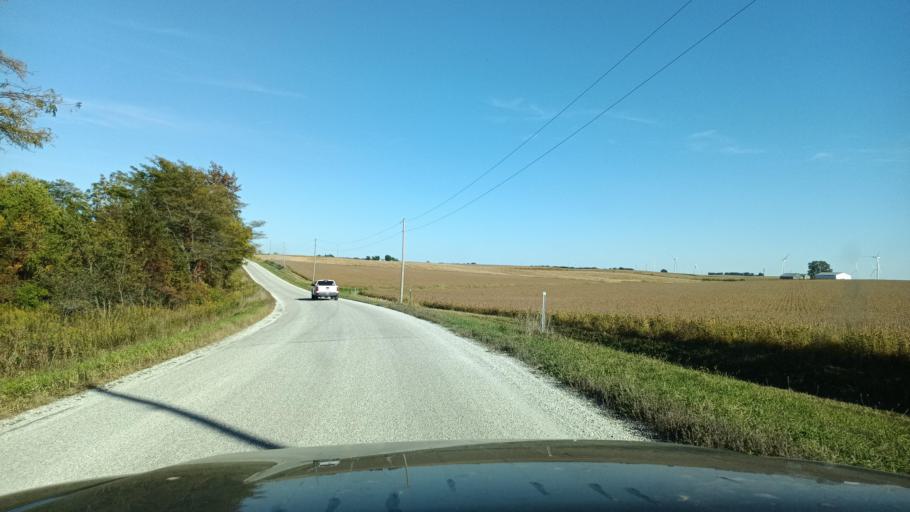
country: US
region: Illinois
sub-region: Logan County
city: Atlanta
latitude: 40.2336
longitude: -89.1558
